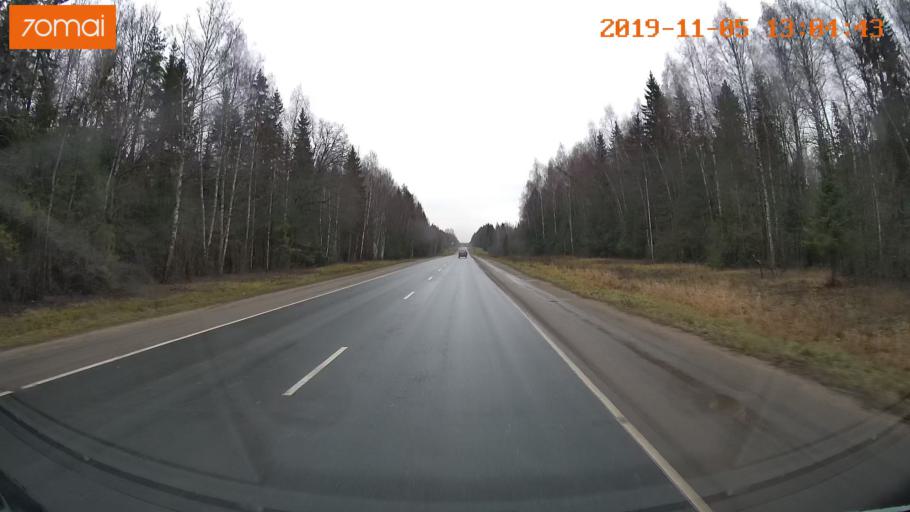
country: RU
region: Ivanovo
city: Kitovo
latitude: 56.8873
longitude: 41.2271
